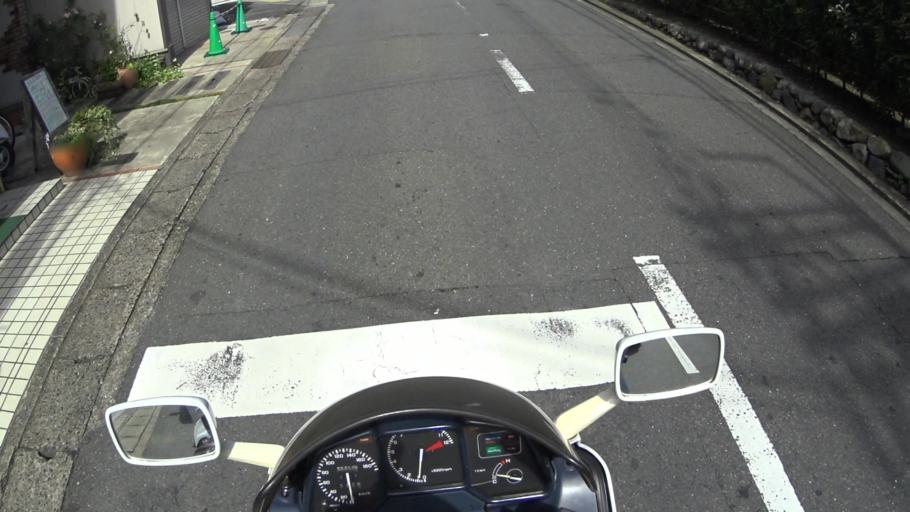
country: JP
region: Shiga Prefecture
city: Otsu-shi
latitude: 34.9603
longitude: 135.8148
